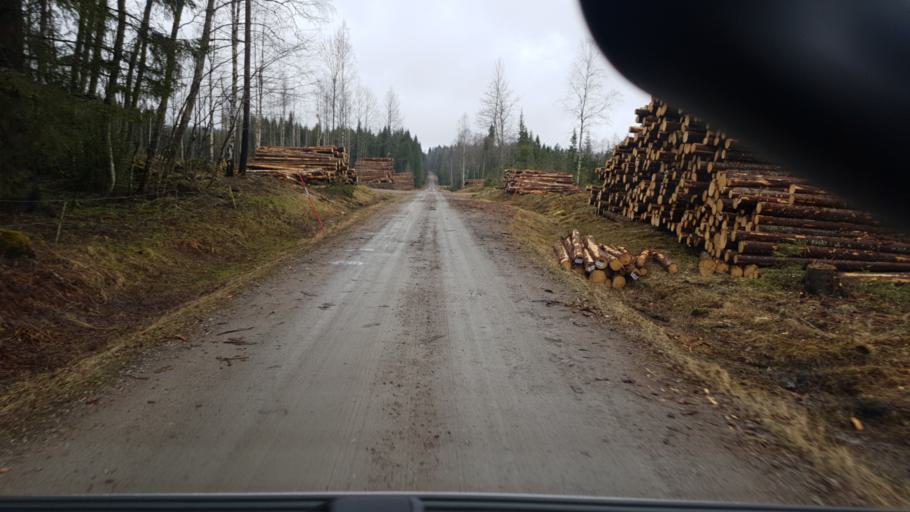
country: SE
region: Vaermland
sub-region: Eda Kommun
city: Charlottenberg
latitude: 59.9873
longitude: 12.5007
